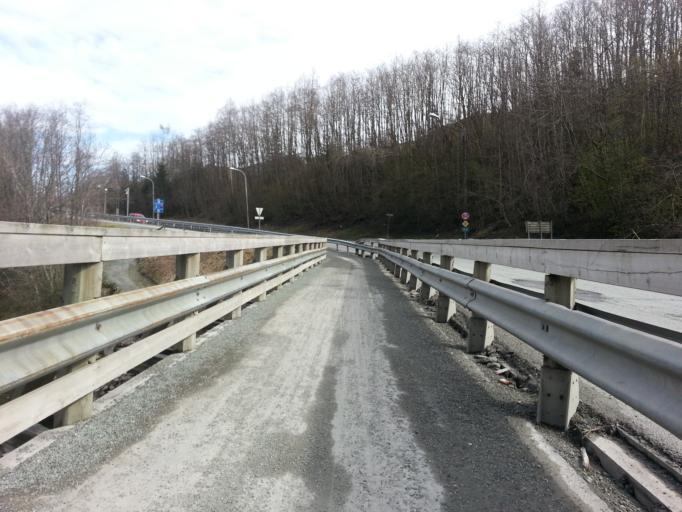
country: NO
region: Sor-Trondelag
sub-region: Trondheim
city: Trondheim
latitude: 63.3957
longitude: 10.3867
